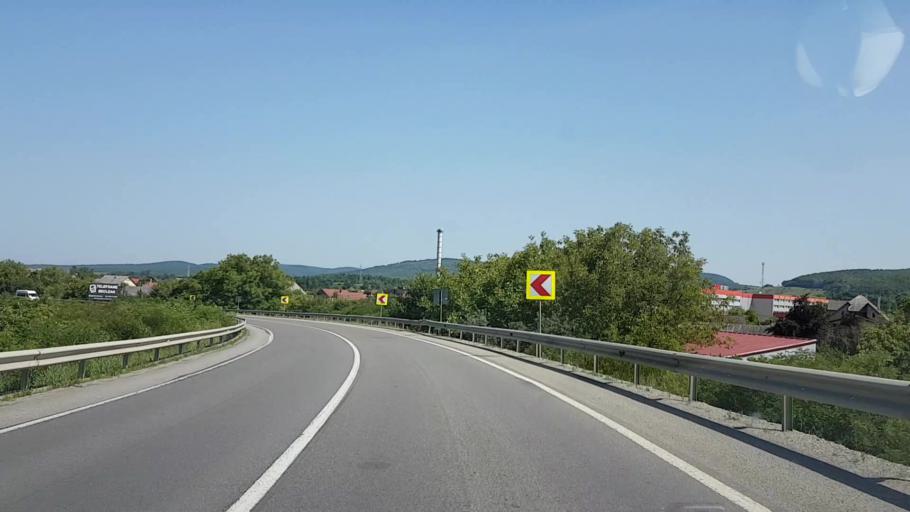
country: RO
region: Bistrita-Nasaud
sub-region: Comuna Beclean
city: Beclean
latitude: 47.1759
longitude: 24.1492
